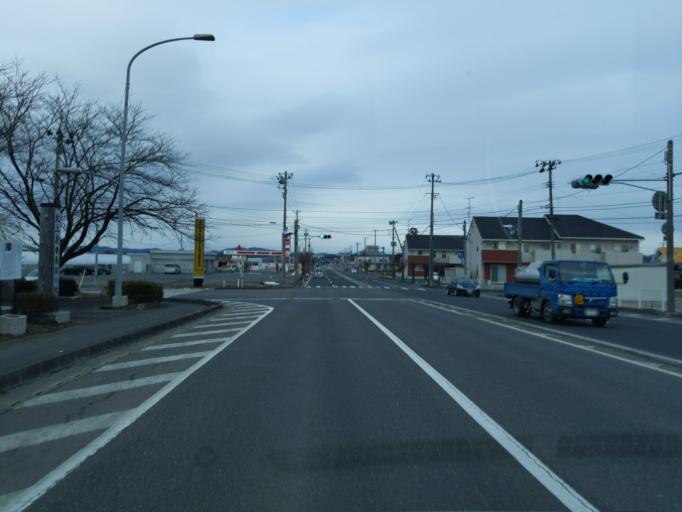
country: JP
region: Iwate
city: Mizusawa
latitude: 39.1729
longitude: 141.1578
